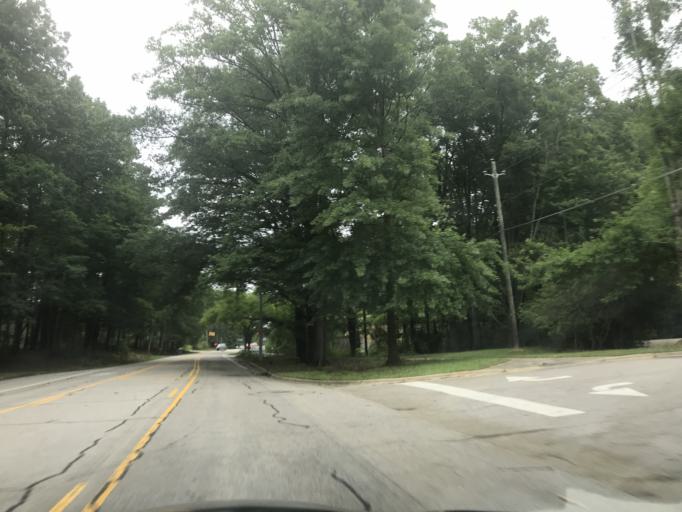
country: US
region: North Carolina
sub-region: Wake County
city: Cary
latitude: 35.7741
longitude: -78.8024
